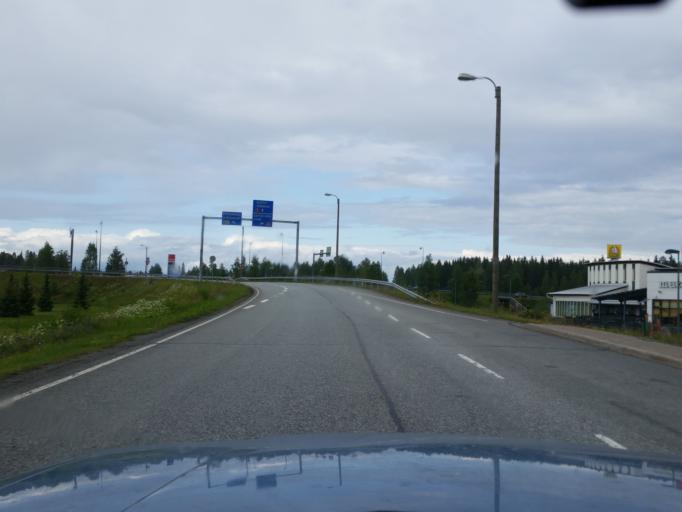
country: FI
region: Southern Savonia
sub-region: Pieksaemaeki
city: Juva
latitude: 61.8974
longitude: 27.8031
